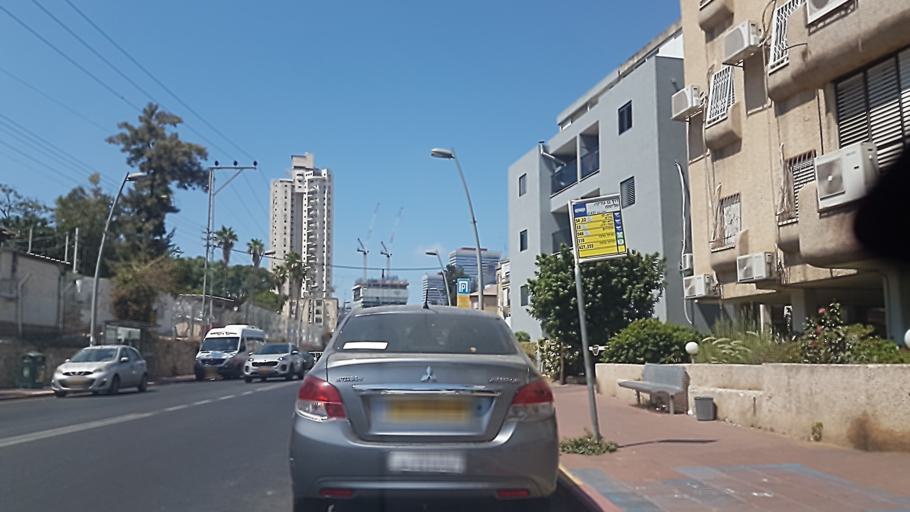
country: IL
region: Tel Aviv
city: Ramat Gan
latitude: 32.0858
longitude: 34.8224
